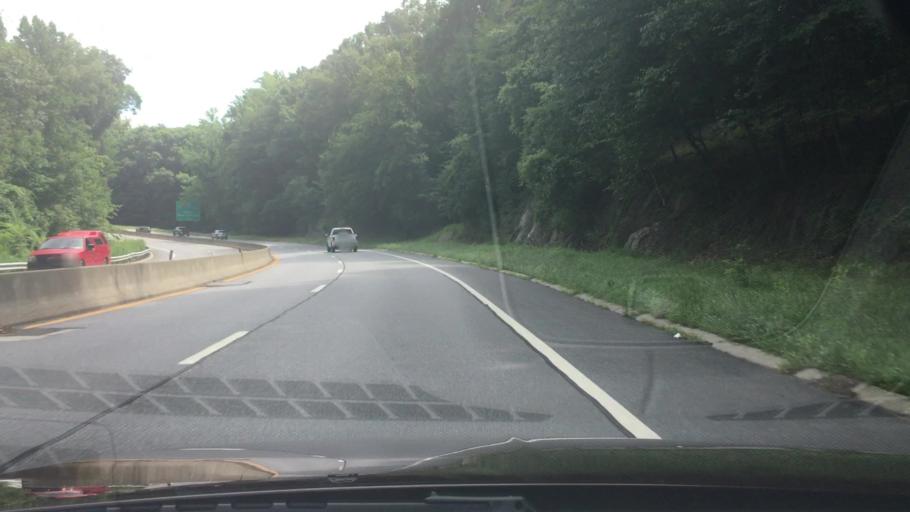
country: US
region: New York
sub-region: Westchester County
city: Elmsford
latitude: 41.0726
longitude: -73.8333
